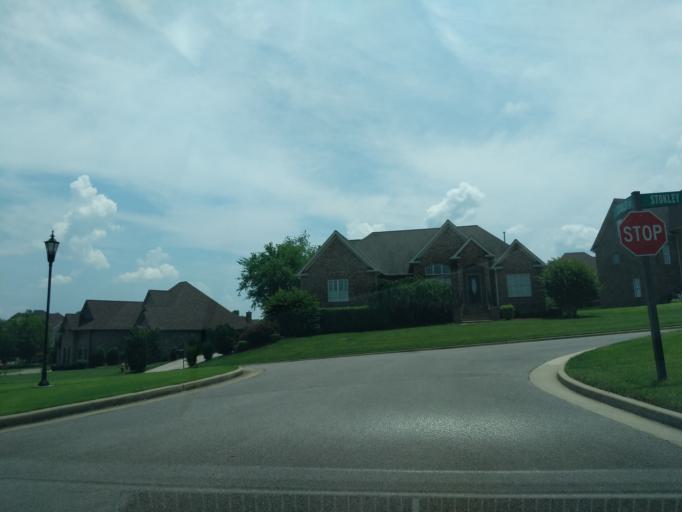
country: US
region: Tennessee
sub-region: Davidson County
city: Lakewood
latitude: 36.2332
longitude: -86.6342
